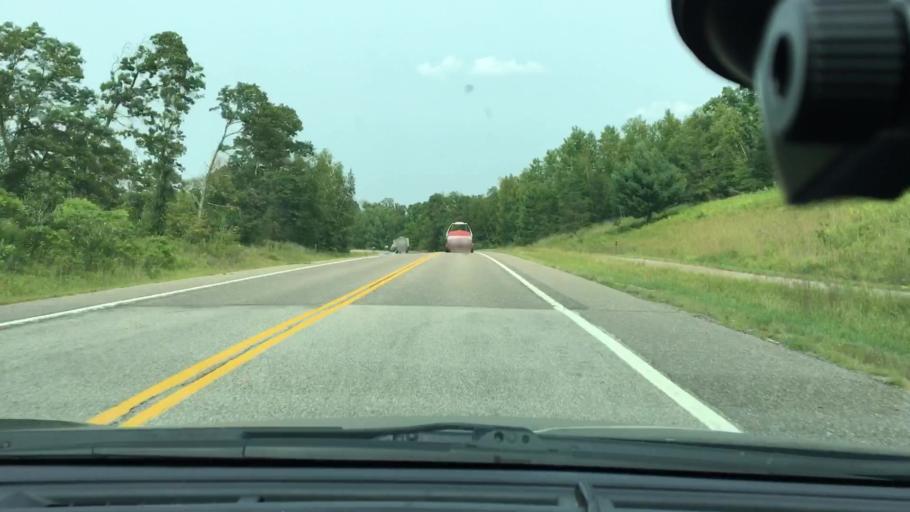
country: US
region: Minnesota
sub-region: Cass County
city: East Gull Lake
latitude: 46.3985
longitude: -94.3510
